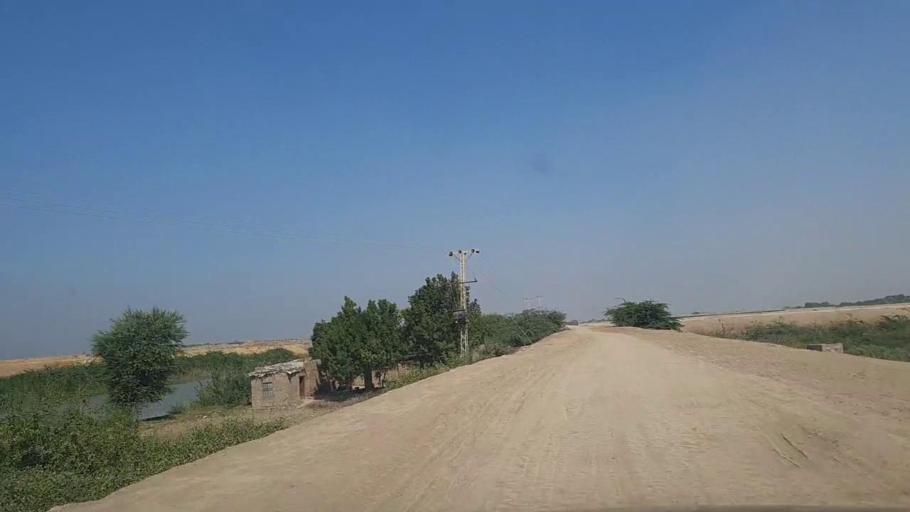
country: PK
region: Sindh
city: Daro Mehar
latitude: 24.8982
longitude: 68.0717
